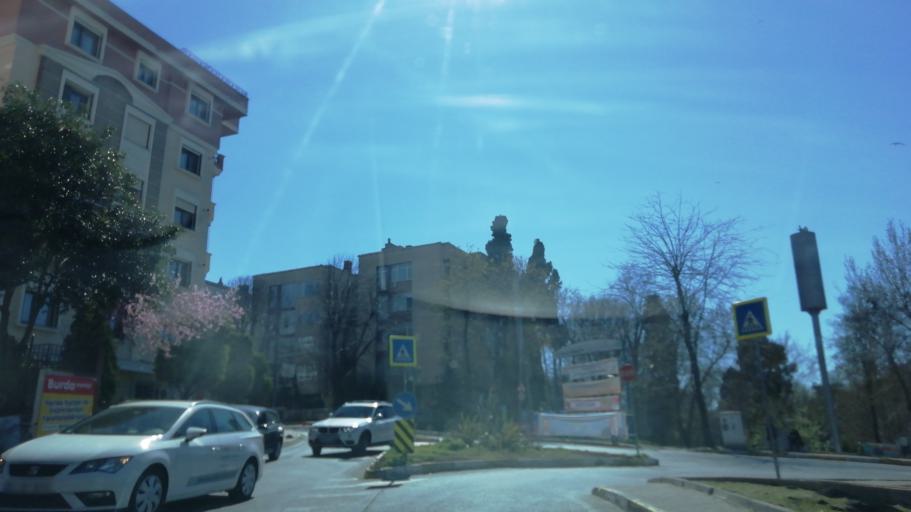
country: TR
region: Istanbul
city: Bahcelievler
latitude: 40.9832
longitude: 28.8674
